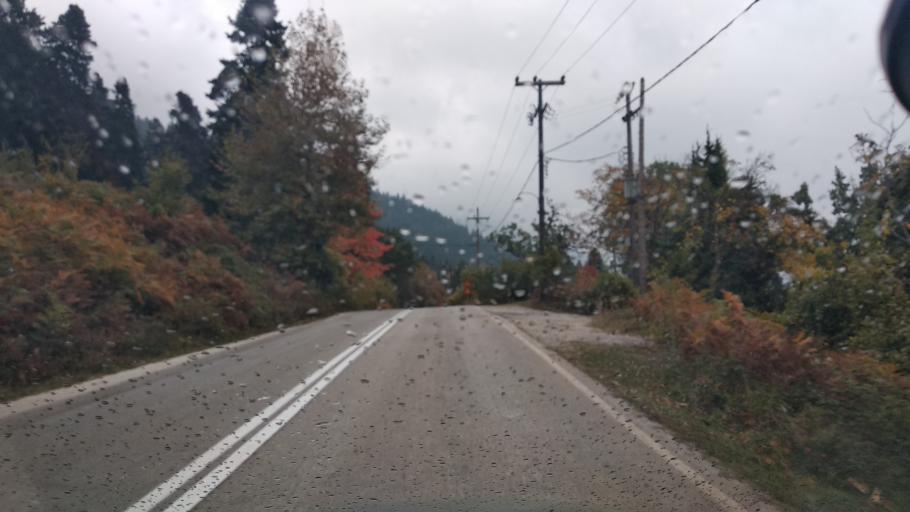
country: GR
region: Thessaly
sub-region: Trikala
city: Pyli
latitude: 39.5139
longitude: 21.5284
